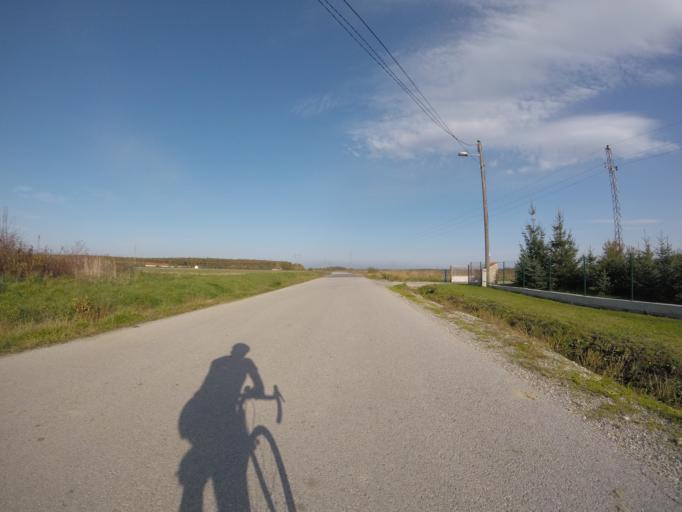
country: HR
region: Zagrebacka
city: Mraclin
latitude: 45.6452
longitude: 16.0617
